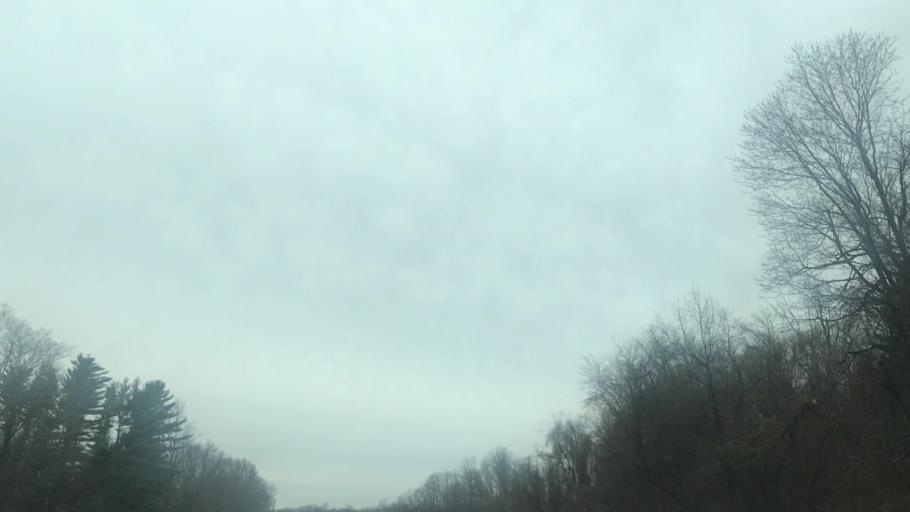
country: US
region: New York
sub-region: Rockland County
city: Chestnut Ridge
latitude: 41.0828
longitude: -74.0469
